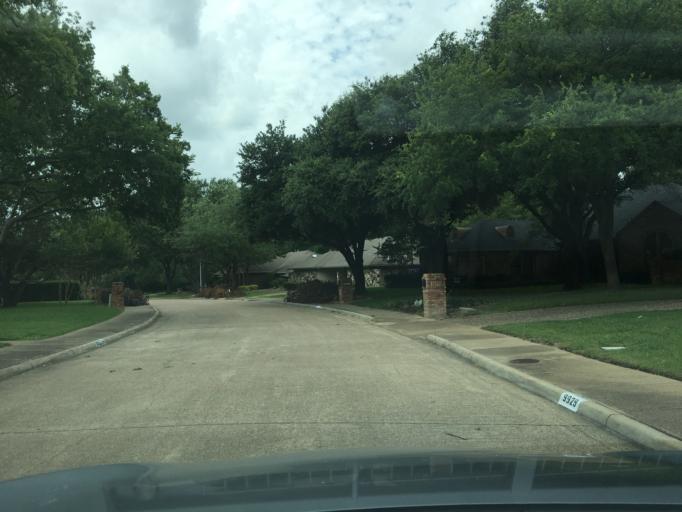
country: US
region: Texas
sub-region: Dallas County
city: Richardson
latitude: 32.9125
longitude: -96.7151
